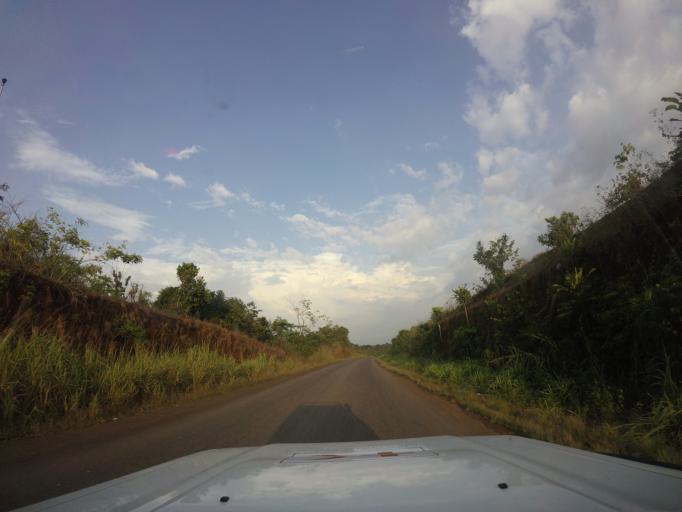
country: LR
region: Bomi
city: Tubmanburg
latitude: 6.7319
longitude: -10.9949
